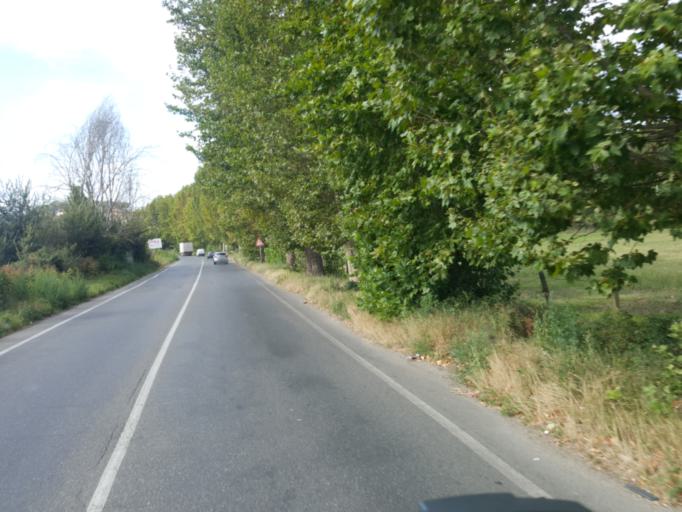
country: IT
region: Latium
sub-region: Citta metropolitana di Roma Capitale
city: Girardi-Bellavista-Terrazze
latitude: 42.1107
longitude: 12.5852
